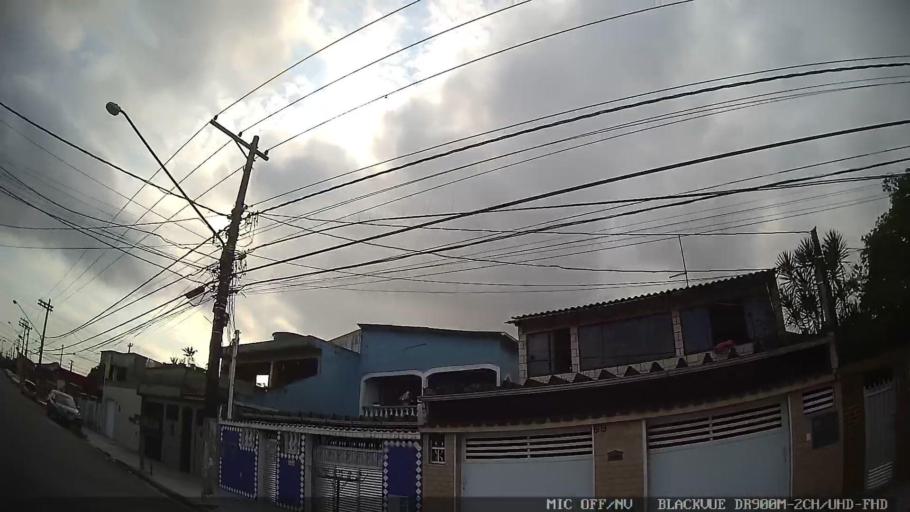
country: BR
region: Sao Paulo
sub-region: Guaruja
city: Guaruja
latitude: -23.9559
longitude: -46.2828
